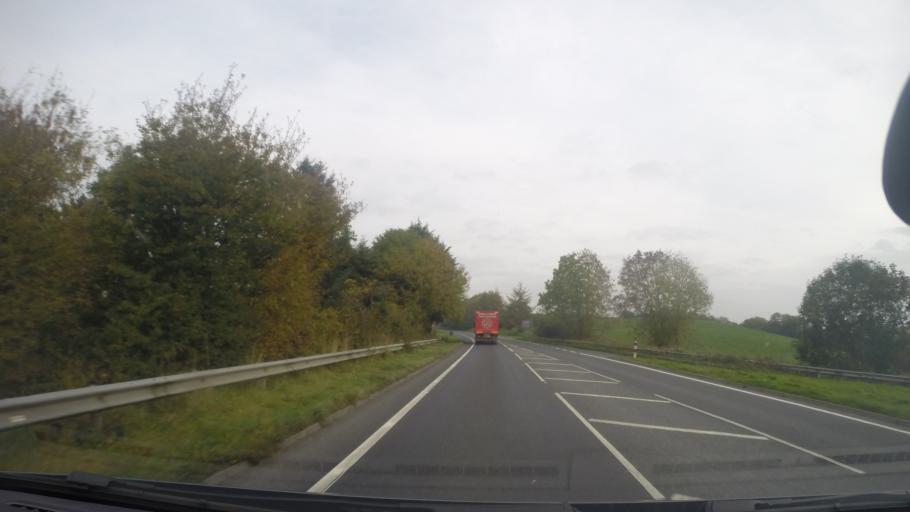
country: GB
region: Northern Ireland
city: Lisnaskea
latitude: 54.2961
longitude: -7.4548
